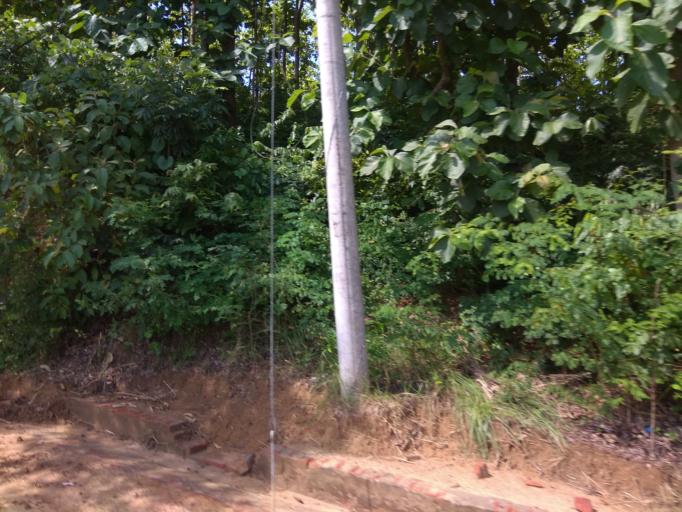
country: BD
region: Chittagong
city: Khagrachhari
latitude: 23.0337
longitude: 92.0082
